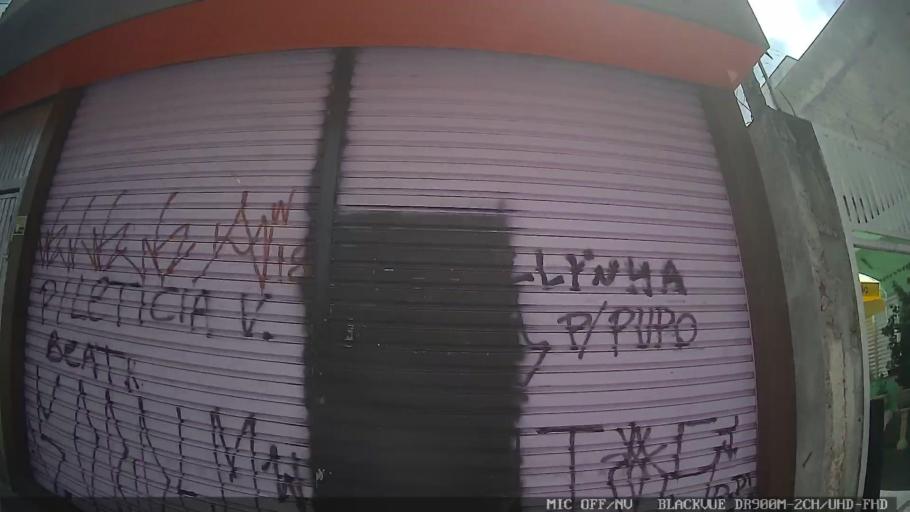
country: BR
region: Sao Paulo
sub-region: Suzano
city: Suzano
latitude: -23.5395
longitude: -46.3091
